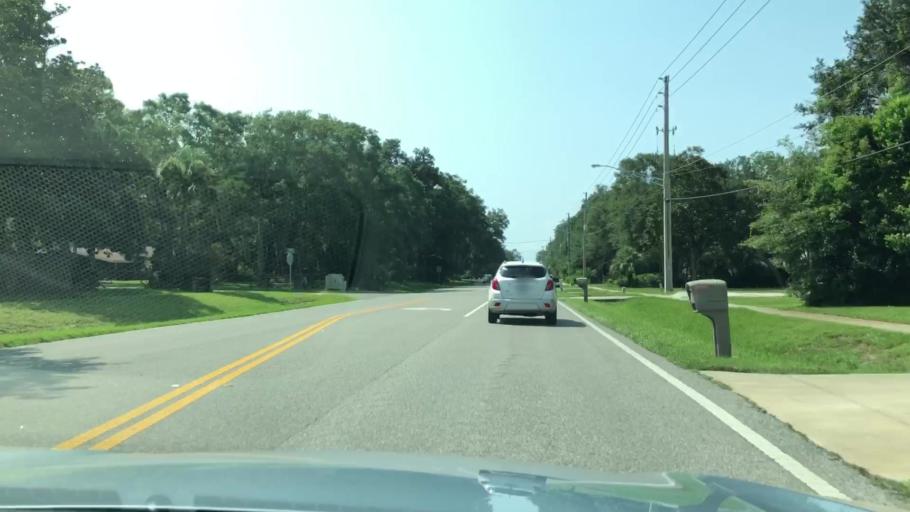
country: US
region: Florida
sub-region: Duval County
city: Neptune Beach
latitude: 30.3193
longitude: -81.4084
